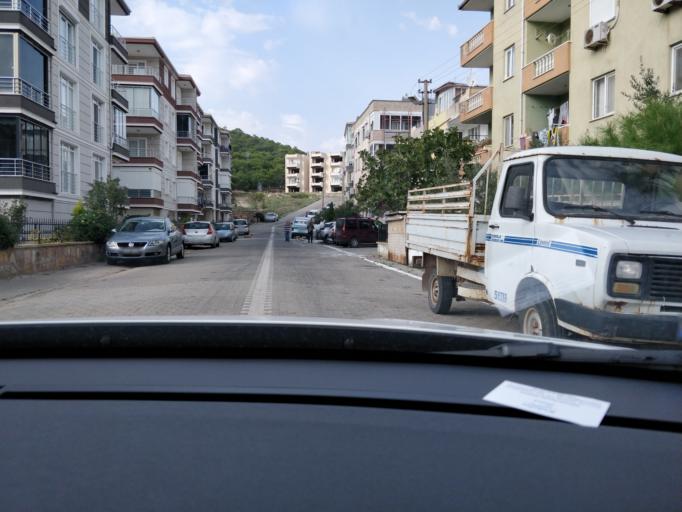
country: TR
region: Balikesir
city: Ayvalik
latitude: 39.2724
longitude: 26.6503
